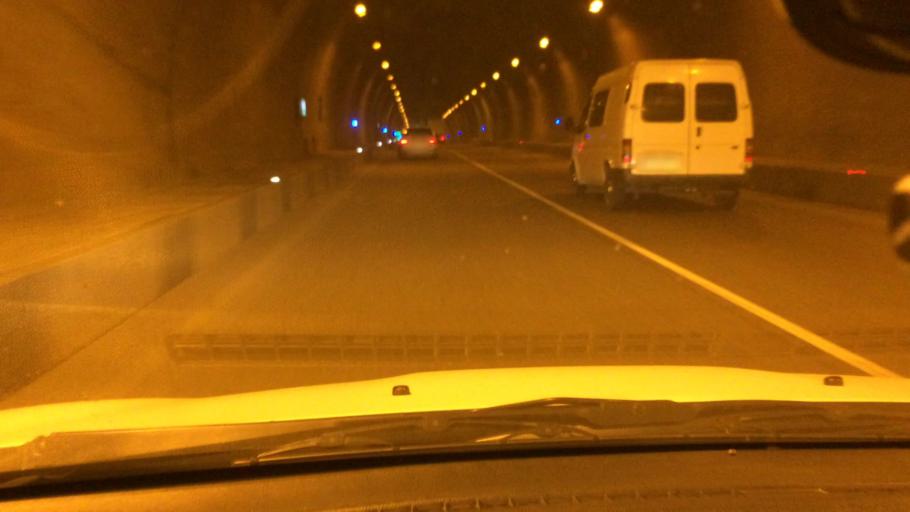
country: GE
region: Ajaria
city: Makhinjauri
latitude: 41.6929
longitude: 41.7228
